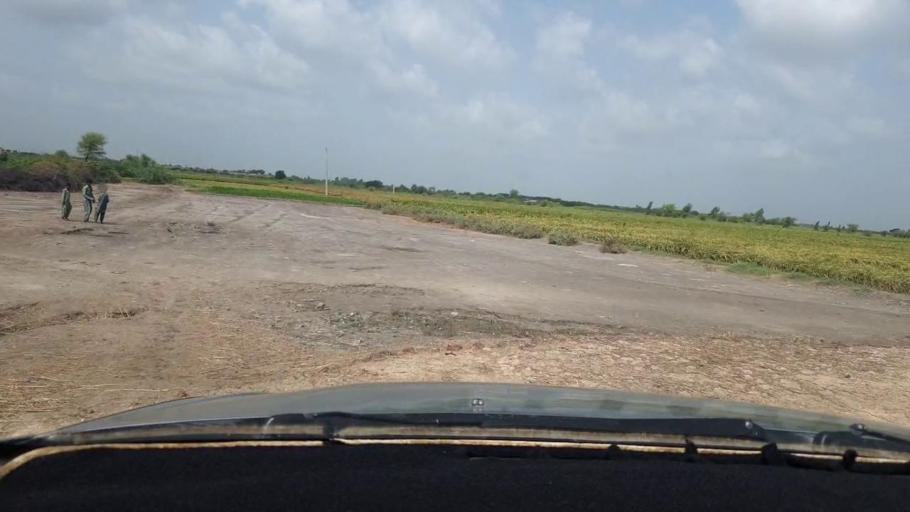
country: PK
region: Sindh
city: Tando Bago
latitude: 24.7572
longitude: 69.0957
